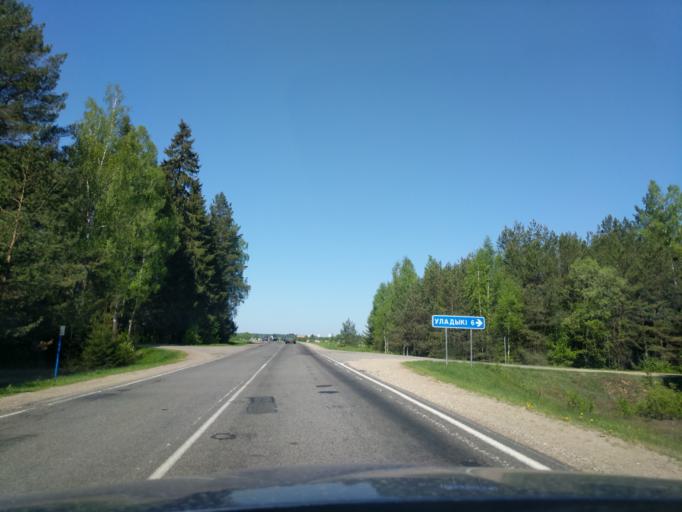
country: BY
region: Minsk
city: Il'ya
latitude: 54.4098
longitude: 27.3073
